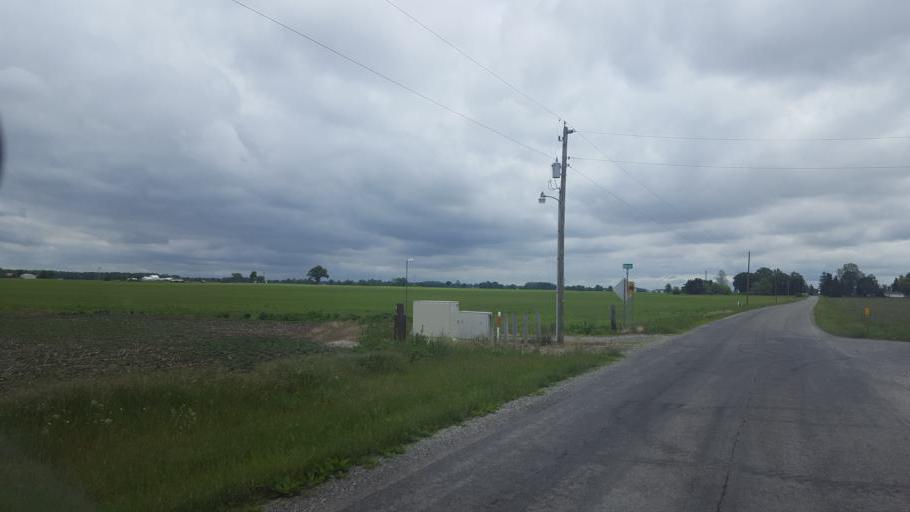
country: US
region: Ohio
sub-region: Crawford County
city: Bucyrus
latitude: 40.7755
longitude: -83.0269
